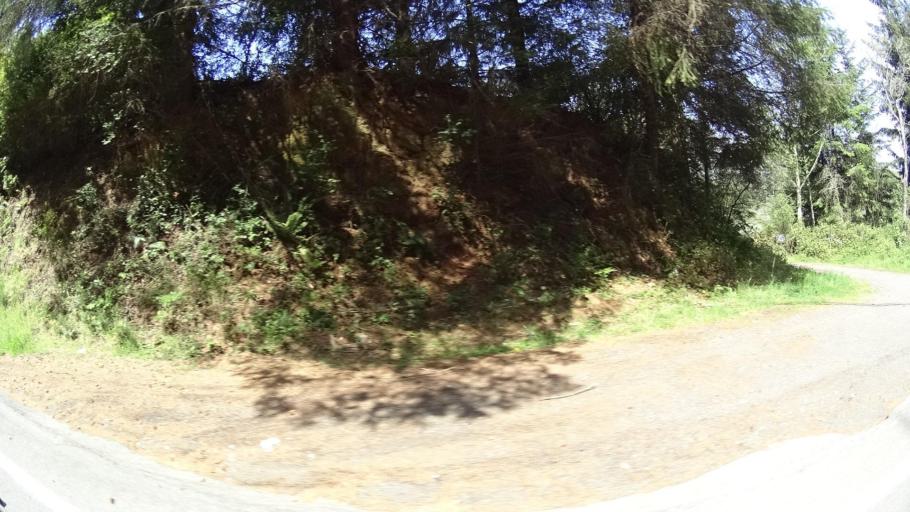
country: US
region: California
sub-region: Humboldt County
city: Humboldt Hill
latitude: 40.6622
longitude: -124.2059
